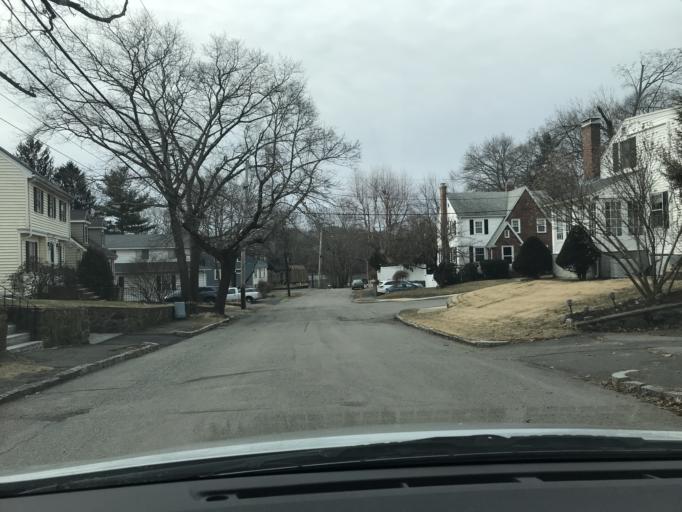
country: US
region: Massachusetts
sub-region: Middlesex County
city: Belmont
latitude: 42.4117
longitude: -71.1759
